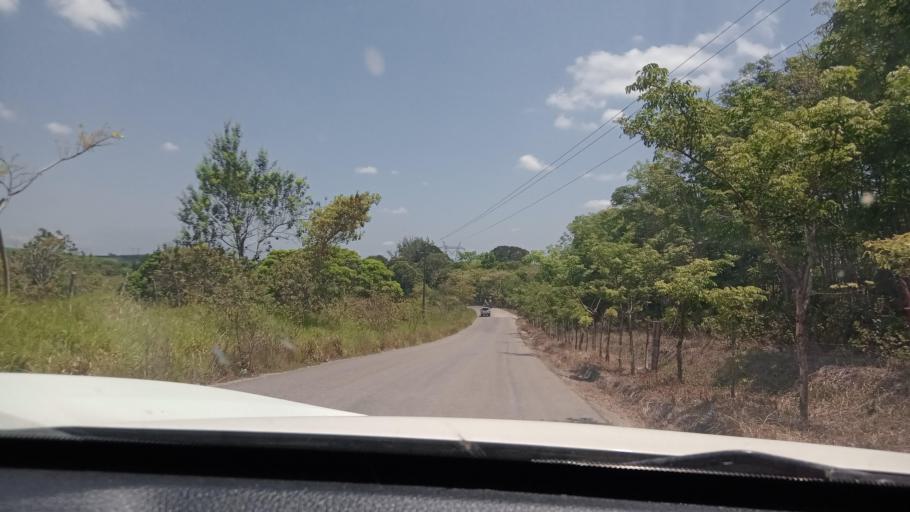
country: MX
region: Veracruz
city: Las Choapas
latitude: 17.7572
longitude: -94.1113
